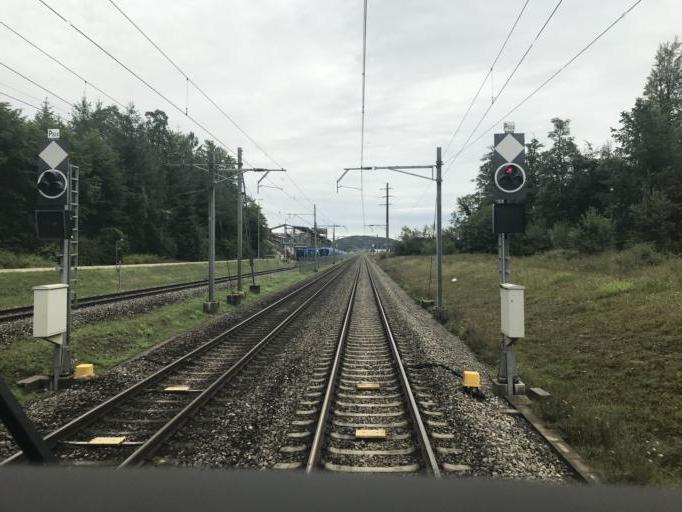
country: CH
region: Zurich
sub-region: Bezirk Buelach
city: Seglingen
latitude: 47.5925
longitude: 8.5251
